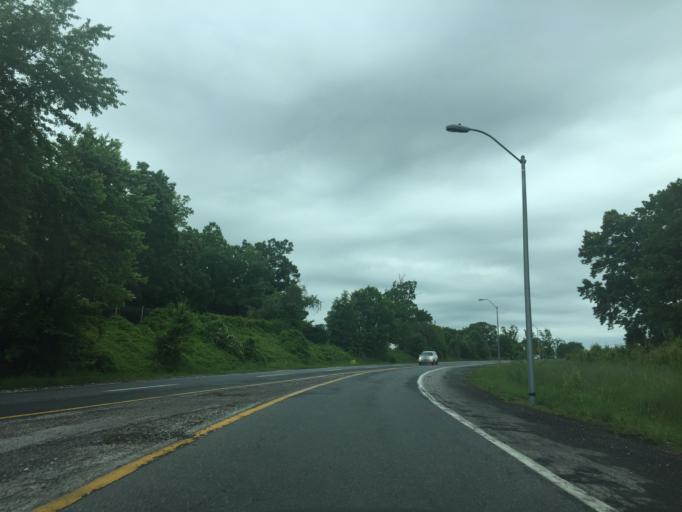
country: US
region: Maryland
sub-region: Baltimore County
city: Rossville
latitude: 39.3718
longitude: -76.4745
